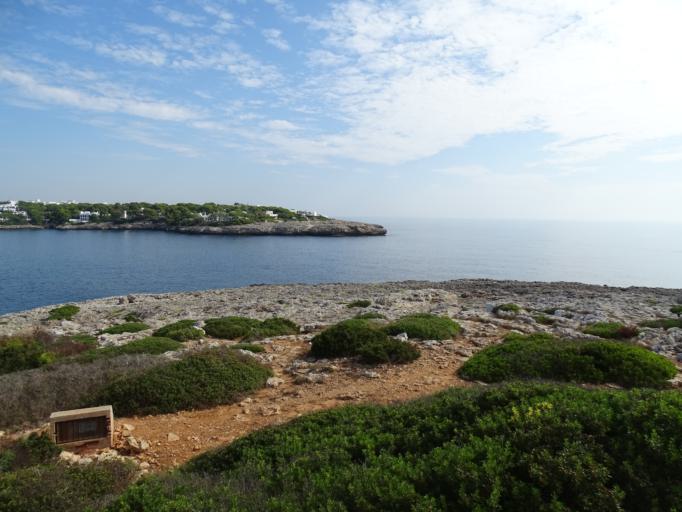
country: ES
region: Balearic Islands
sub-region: Illes Balears
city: Santanyi
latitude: 39.3668
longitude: 3.2340
